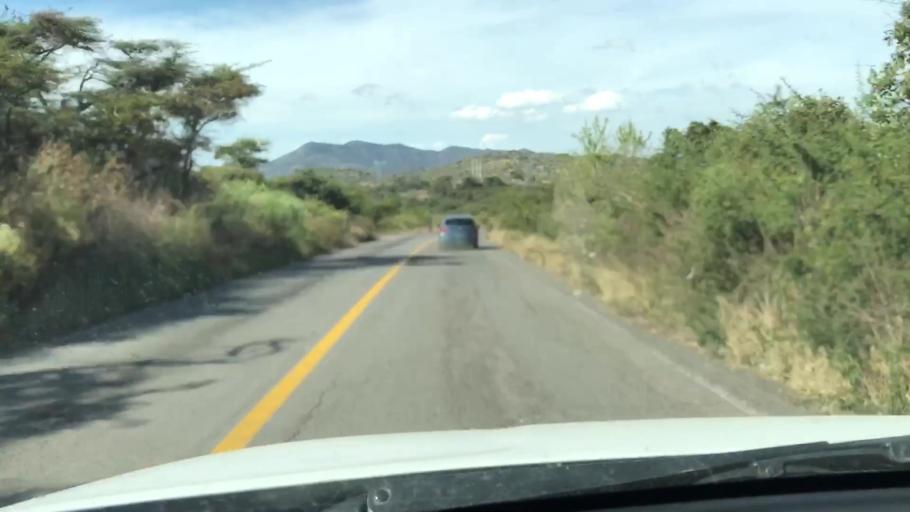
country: MX
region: Jalisco
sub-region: Zacoalco de Torres
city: Barranca de Otates (Barranca de Otatan)
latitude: 20.2049
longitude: -103.6912
